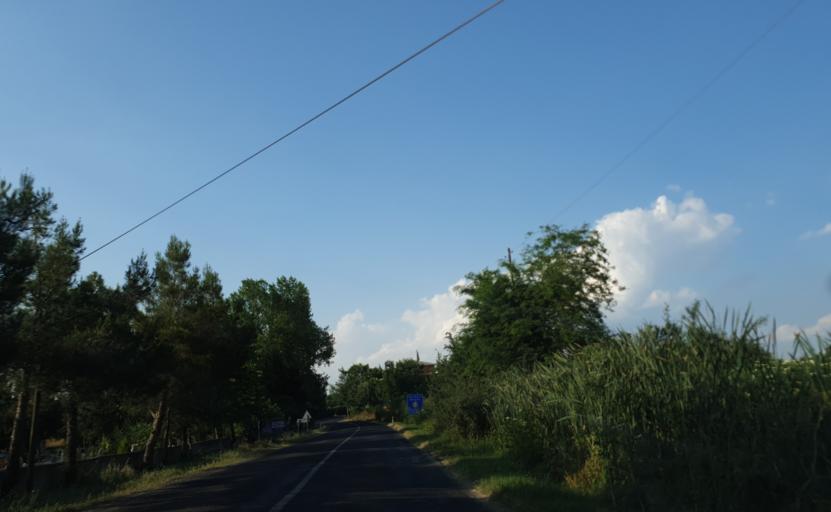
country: TR
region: Tekirdag
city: Muratli
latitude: 41.1987
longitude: 27.4700
